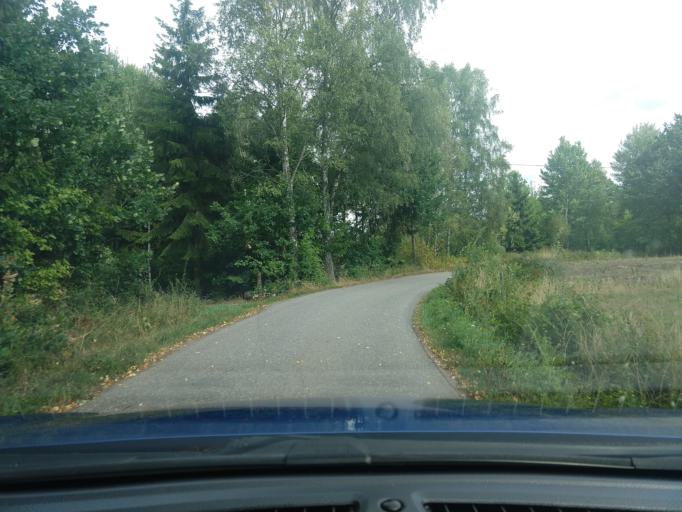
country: SE
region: Blekinge
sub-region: Ronneby Kommun
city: Brakne-Hoby
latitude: 56.2867
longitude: 15.1899
